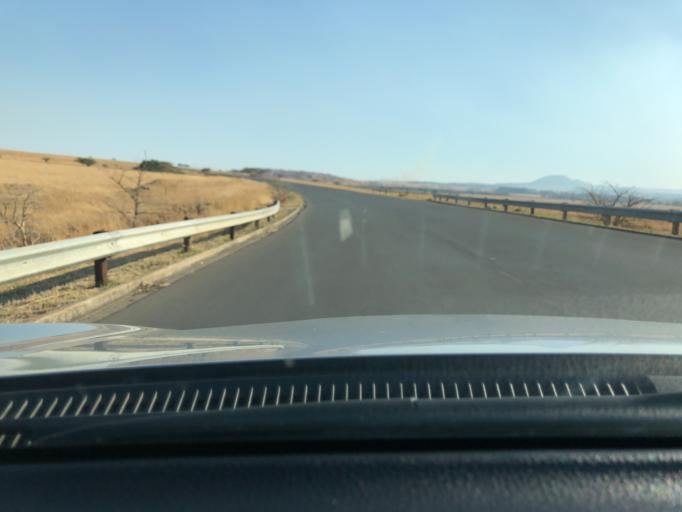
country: ZA
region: KwaZulu-Natal
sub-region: uThukela District Municipality
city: Ekuvukeni
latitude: -28.3503
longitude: 30.0251
